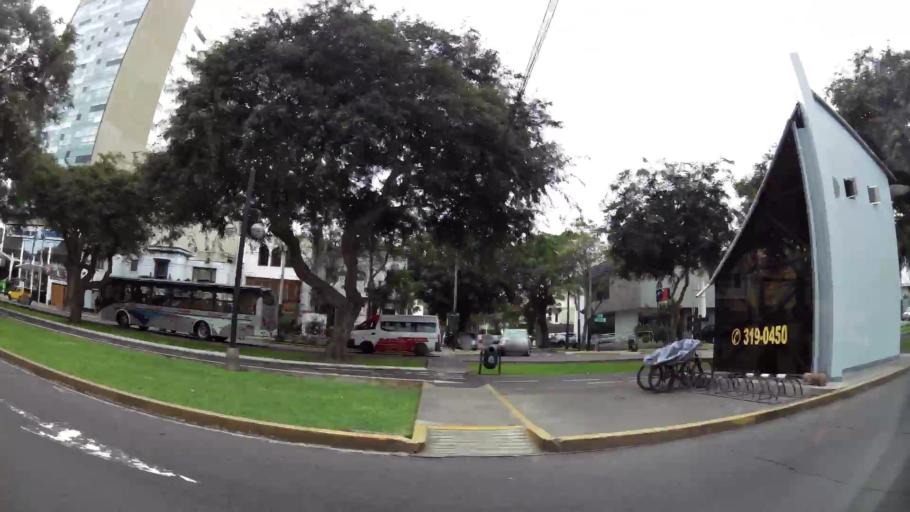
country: PE
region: Lima
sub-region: Lima
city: San Isidro
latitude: -12.0970
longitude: -77.0552
